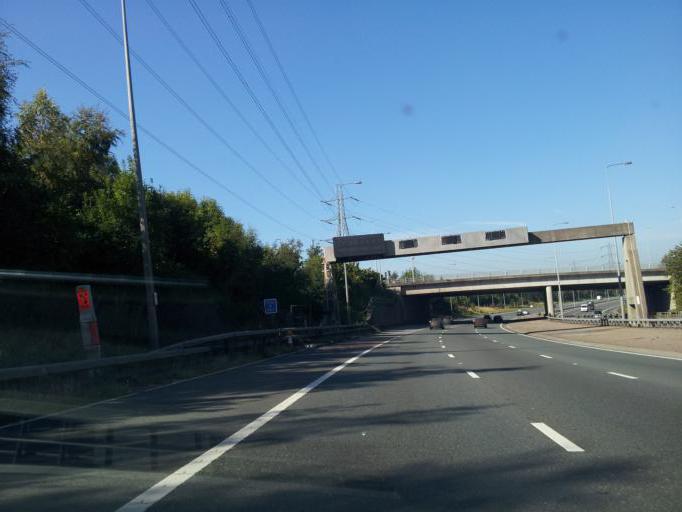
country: GB
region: England
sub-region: Manchester
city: Blackley
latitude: 53.5330
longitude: -2.2058
